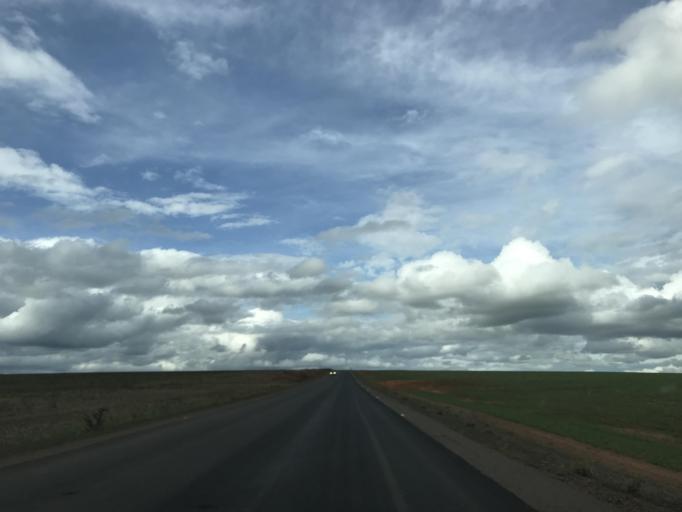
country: BR
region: Goias
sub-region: Vianopolis
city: Vianopolis
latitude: -16.9772
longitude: -48.6639
